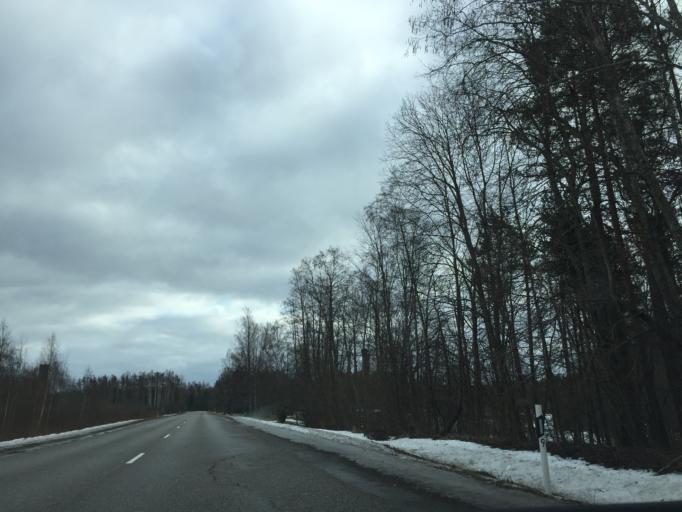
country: LV
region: Salacgrivas
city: Ainazi
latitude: 57.8584
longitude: 24.5096
